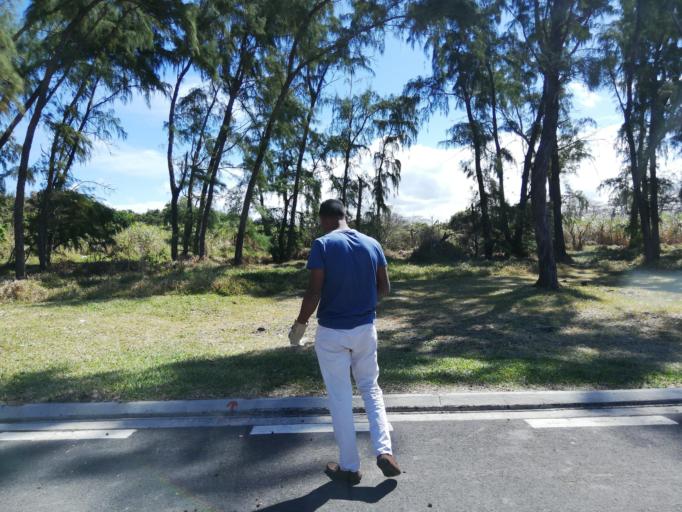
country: MU
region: Grand Port
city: Beau Vallon
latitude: -20.4538
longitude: 57.6978
